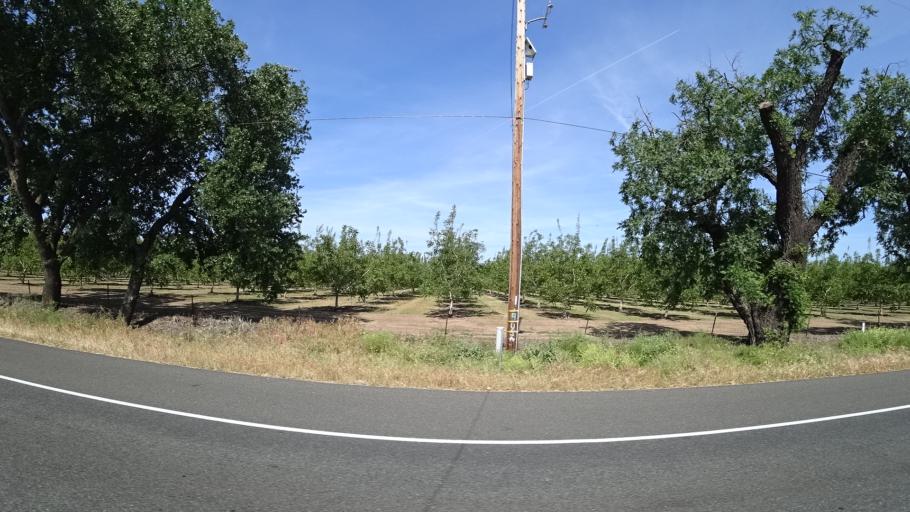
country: US
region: California
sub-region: Tehama County
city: Red Bluff
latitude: 40.1793
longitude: -122.1714
